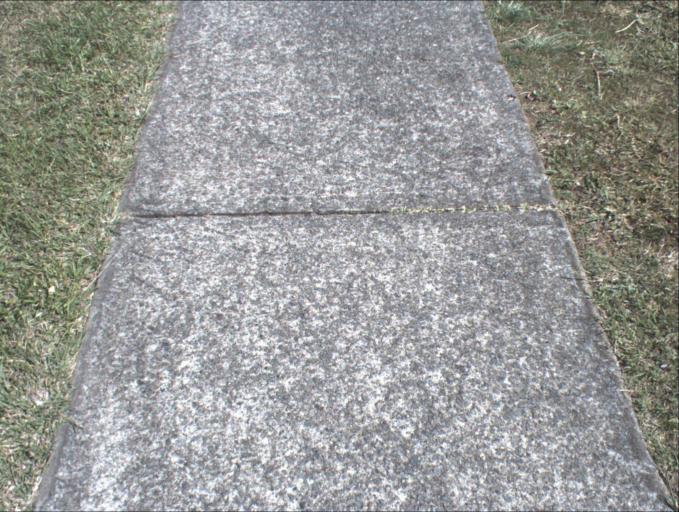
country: AU
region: Queensland
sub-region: Logan
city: Rochedale South
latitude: -27.5971
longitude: 153.1090
